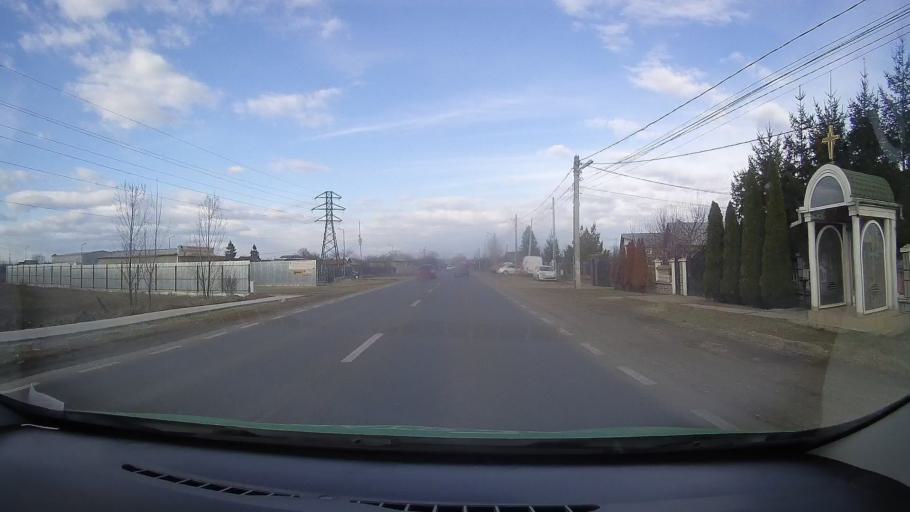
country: RO
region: Dambovita
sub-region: Comuna Ulmi
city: Viisoara
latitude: 44.8874
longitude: 25.4335
